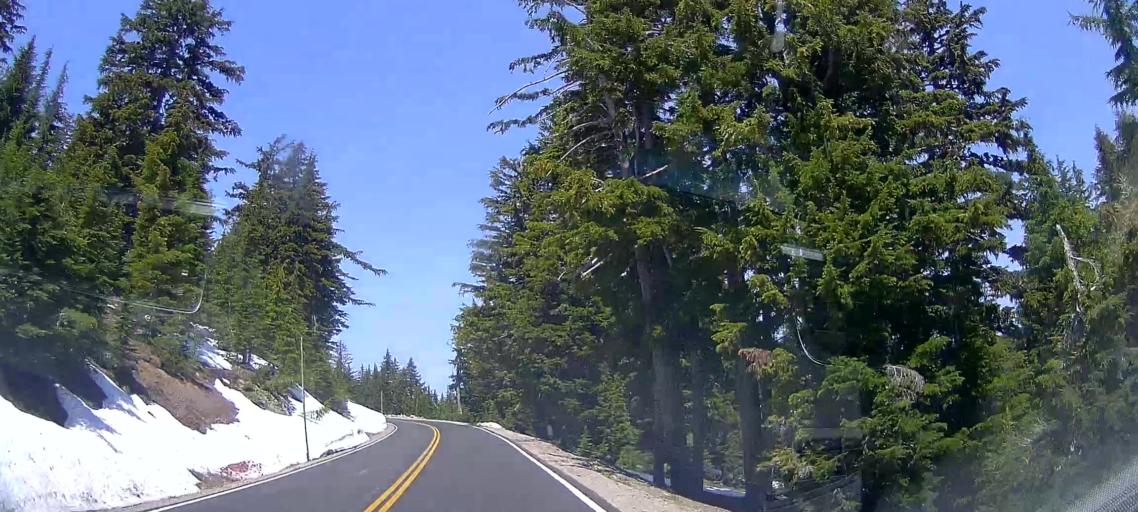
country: US
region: Oregon
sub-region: Jackson County
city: Shady Cove
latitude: 42.9814
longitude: -122.1301
